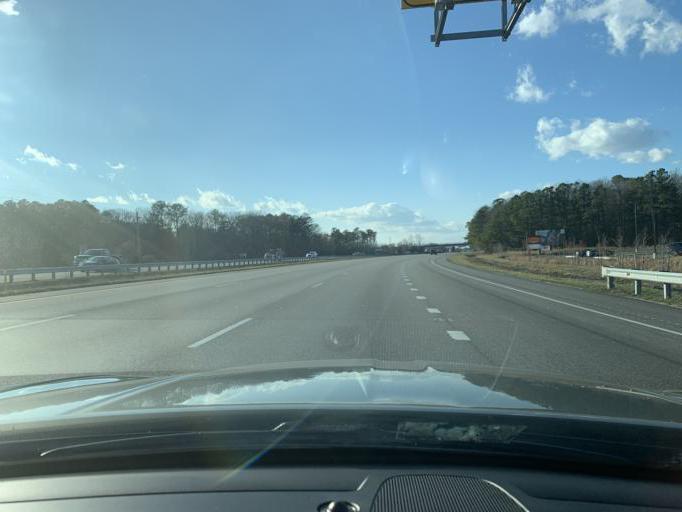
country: US
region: Maryland
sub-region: Queen Anne's County
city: Grasonville
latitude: 38.9619
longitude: -76.2058
